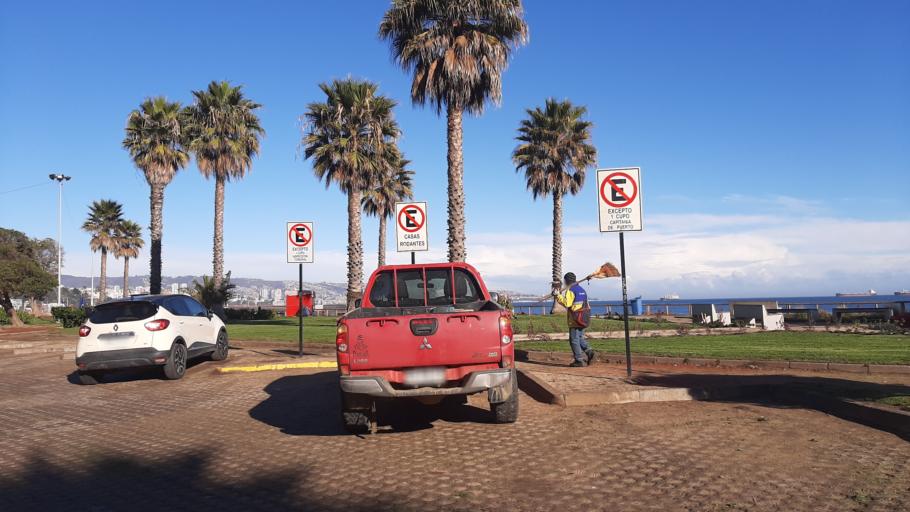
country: CL
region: Valparaiso
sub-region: Provincia de Valparaiso
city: Vina del Mar
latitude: -33.0095
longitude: -71.5519
